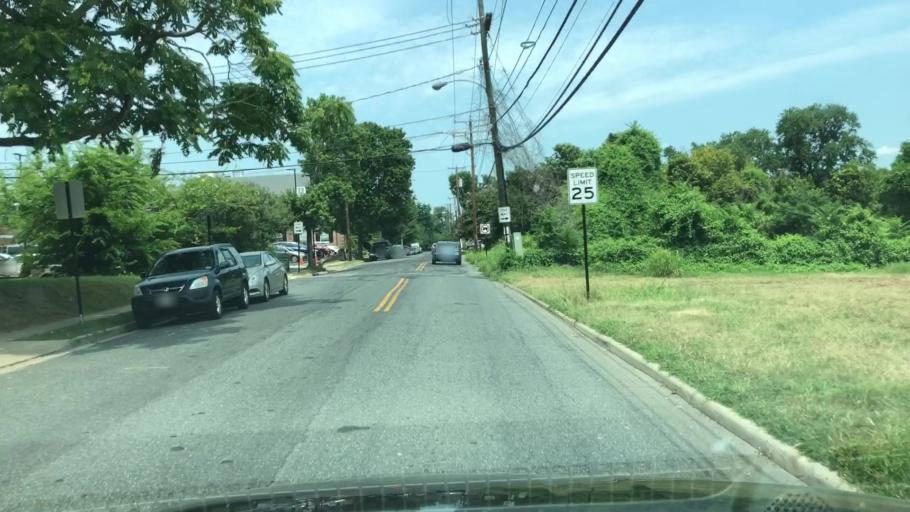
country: US
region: Virginia
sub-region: City of Fredericksburg
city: Fredericksburg
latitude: 38.3058
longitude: -77.4597
